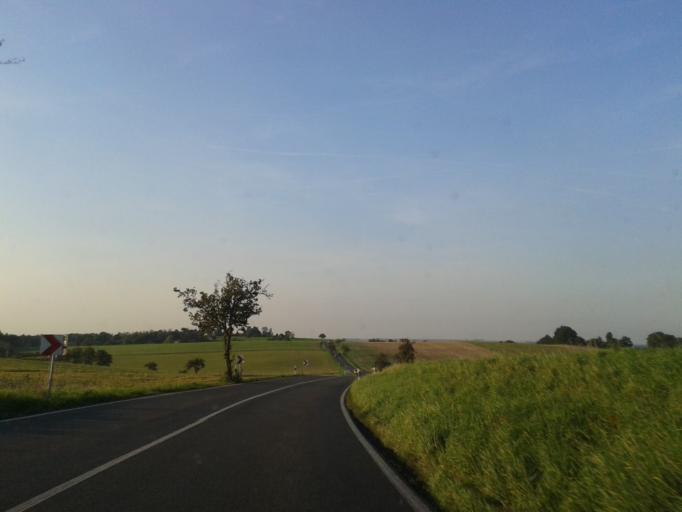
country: DE
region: Saxony
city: Meissen
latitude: 51.1330
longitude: 13.4749
